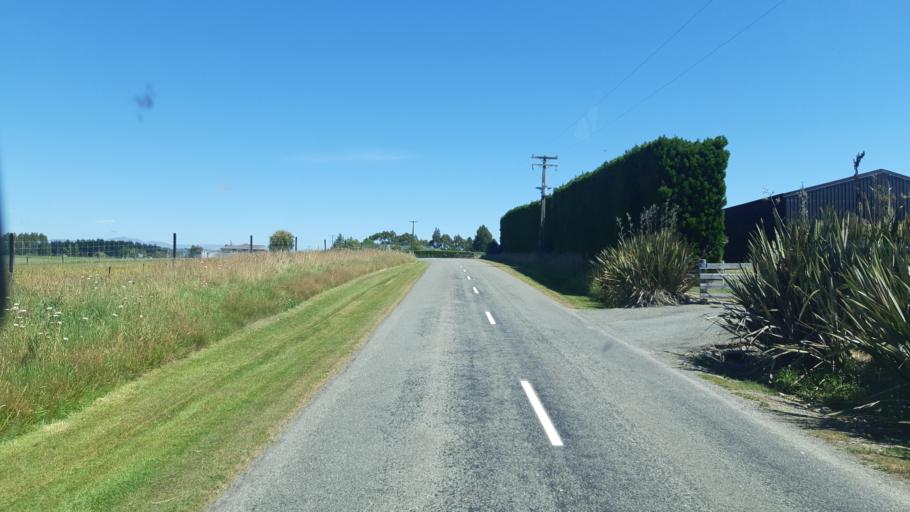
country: NZ
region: Canterbury
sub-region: Timaru District
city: Timaru
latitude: -44.3954
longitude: 171.1586
